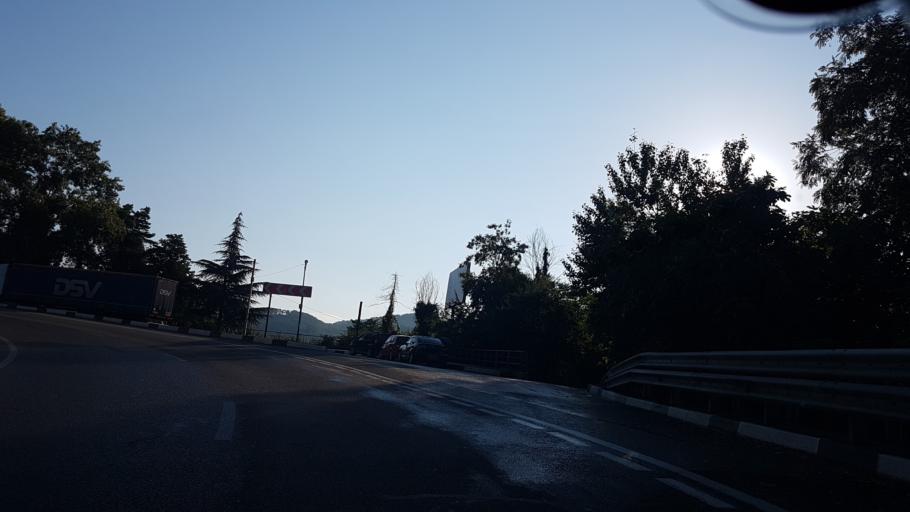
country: RU
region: Krasnodarskiy
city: Dagomys
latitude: 43.6430
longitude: 39.7015
